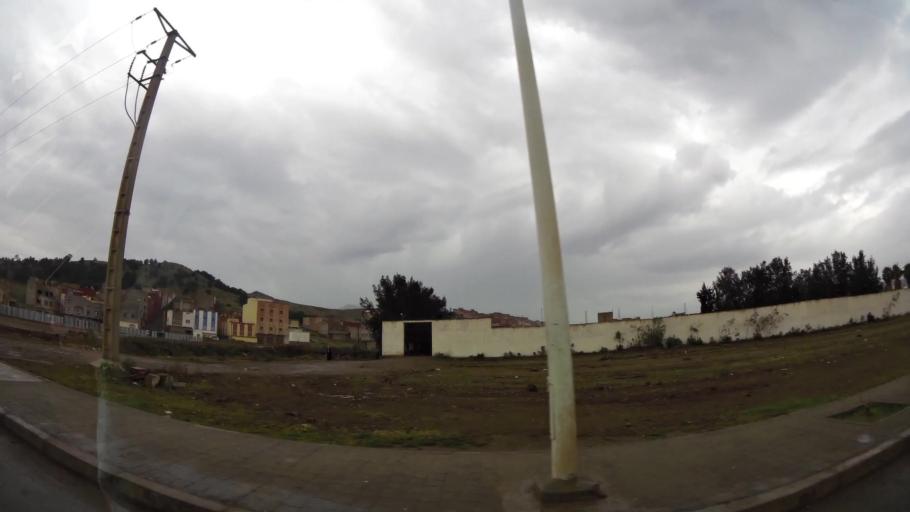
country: MA
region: Oriental
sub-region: Nador
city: Nador
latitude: 35.1487
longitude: -2.9790
